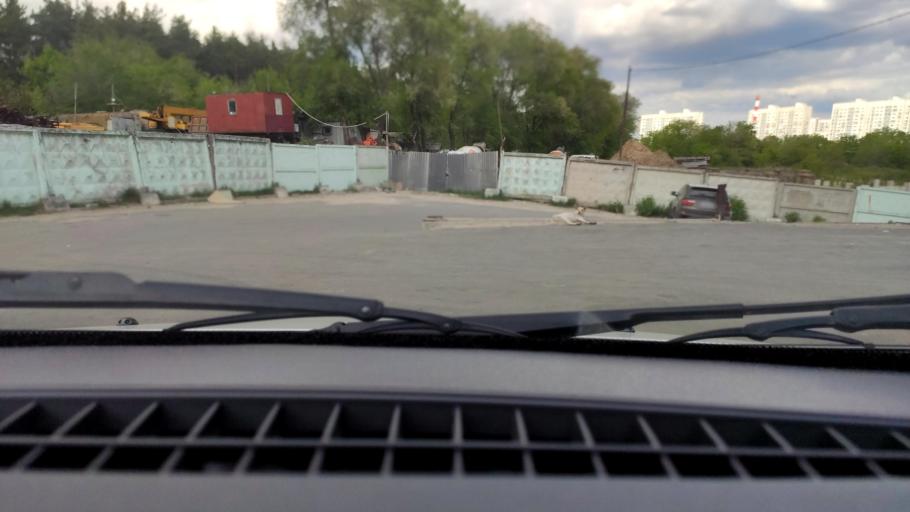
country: RU
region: Voronezj
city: Pridonskoy
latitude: 51.6727
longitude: 39.1232
